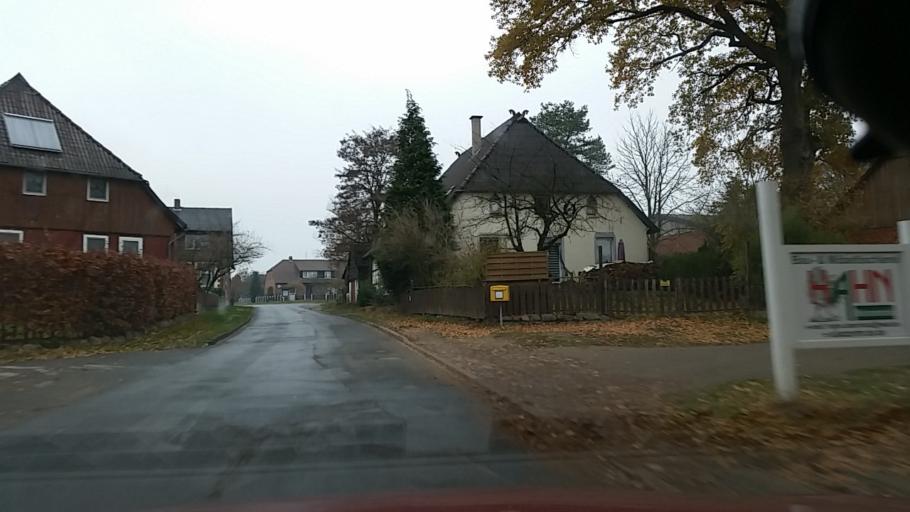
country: DE
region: Lower Saxony
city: Obernholz
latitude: 52.7659
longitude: 10.5969
